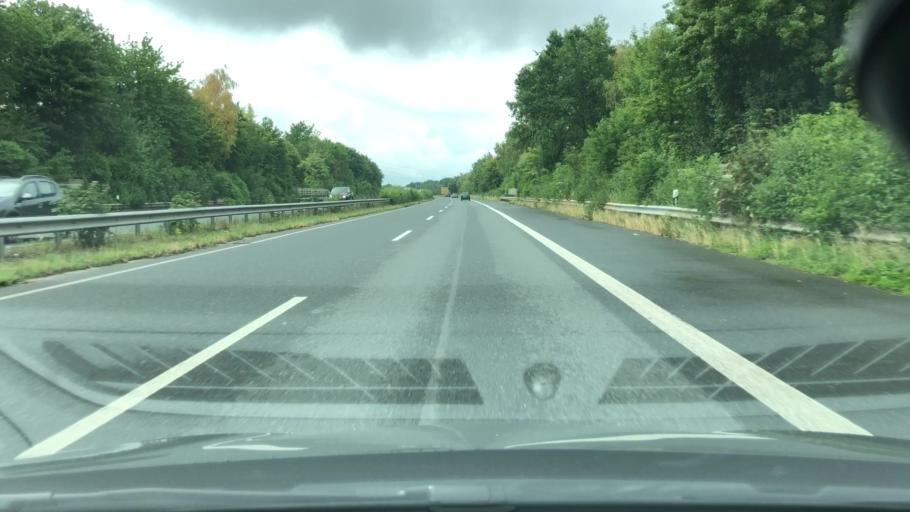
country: DE
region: North Rhine-Westphalia
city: Porta Westfalica
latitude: 52.2682
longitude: 8.9711
